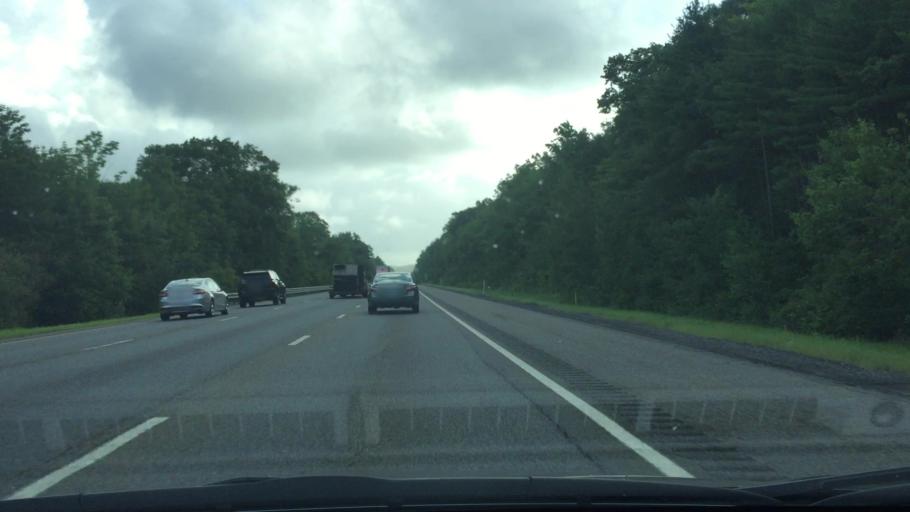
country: US
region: Massachusetts
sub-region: Worcester County
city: Harvard
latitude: 42.4584
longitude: -71.5719
